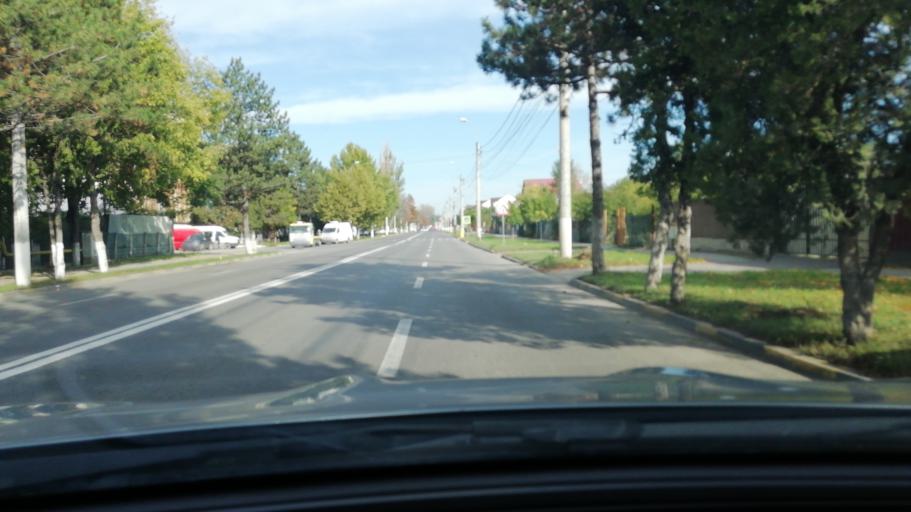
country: RO
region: Galati
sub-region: Municipiul Tecuci
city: Tecuci
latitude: 45.8228
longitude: 27.4386
